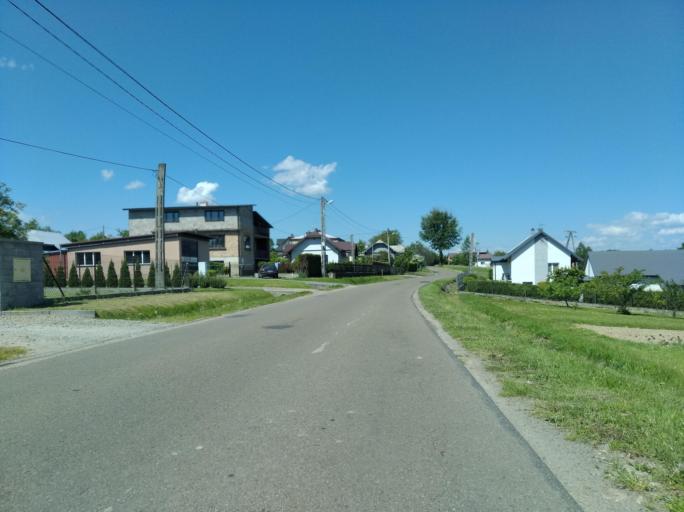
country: PL
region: Subcarpathian Voivodeship
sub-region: Powiat jasielski
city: Tarnowiec
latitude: 49.7116
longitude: 21.6087
